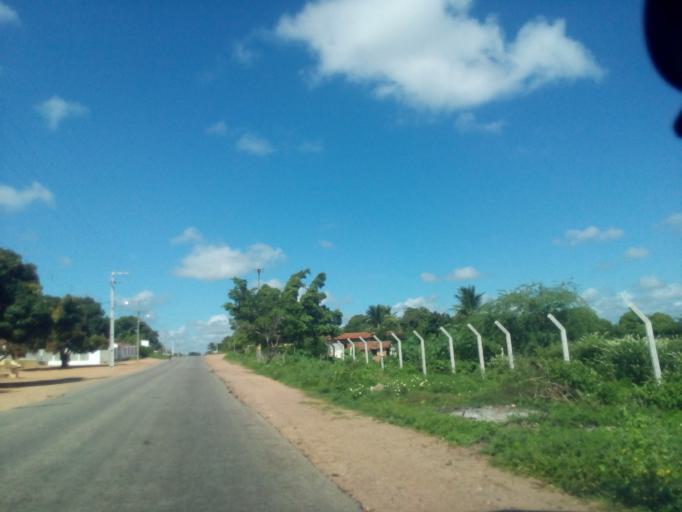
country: BR
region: Rio Grande do Norte
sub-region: Sao Paulo Do Potengi
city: Sao Paulo do Potengi
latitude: -5.9128
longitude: -35.7036
